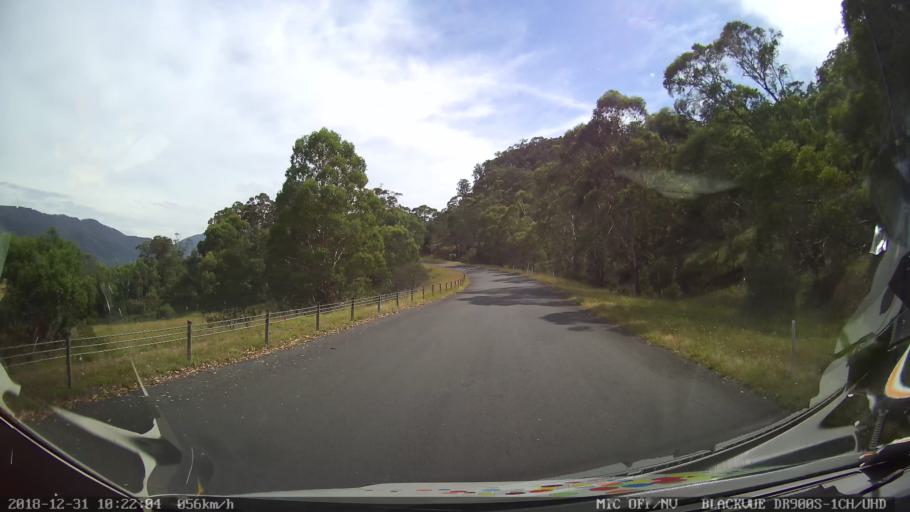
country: AU
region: New South Wales
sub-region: Snowy River
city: Jindabyne
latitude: -36.5288
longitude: 148.1426
